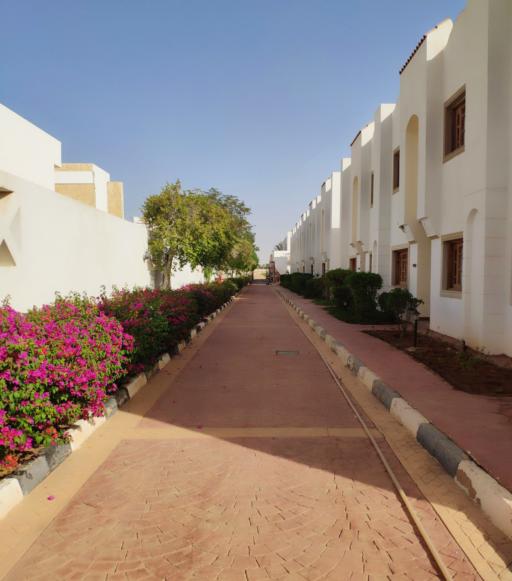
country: EG
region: South Sinai
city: Sharm el-Sheikh
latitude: 27.8640
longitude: 34.3089
